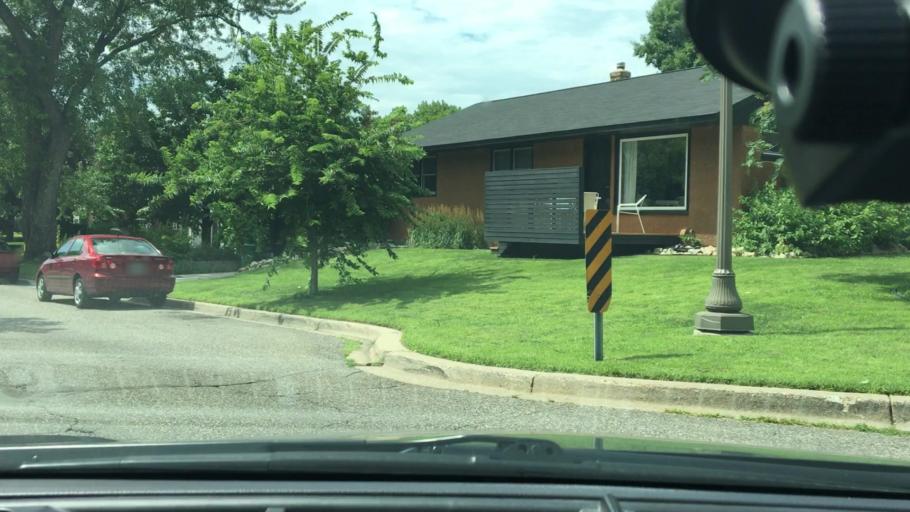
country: US
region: Minnesota
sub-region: Dakota County
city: Mendota Heights
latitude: 44.9198
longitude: -93.1970
